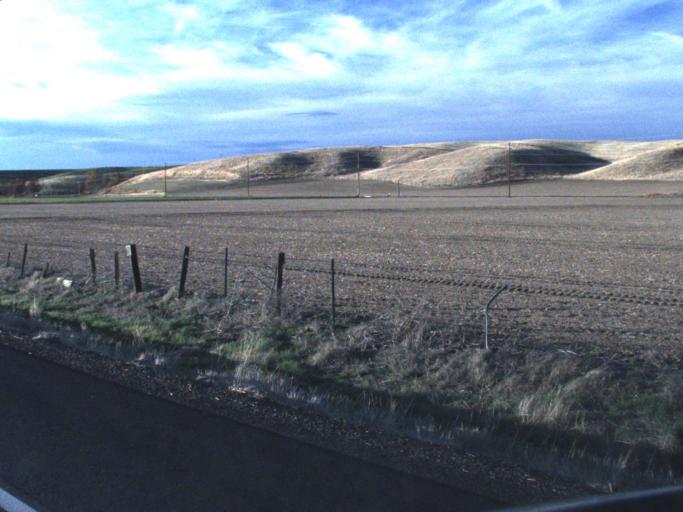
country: US
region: Washington
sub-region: Walla Walla County
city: Garrett
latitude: 46.0510
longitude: -118.5367
